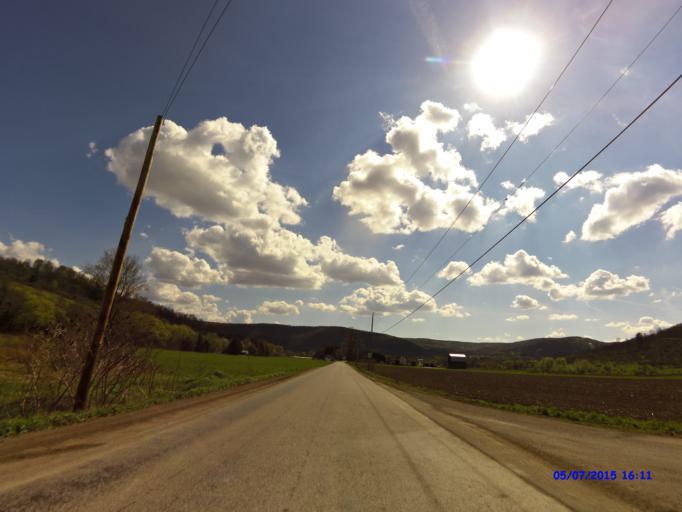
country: US
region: New York
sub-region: Cattaraugus County
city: Salamanca
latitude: 42.2616
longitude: -78.6351
